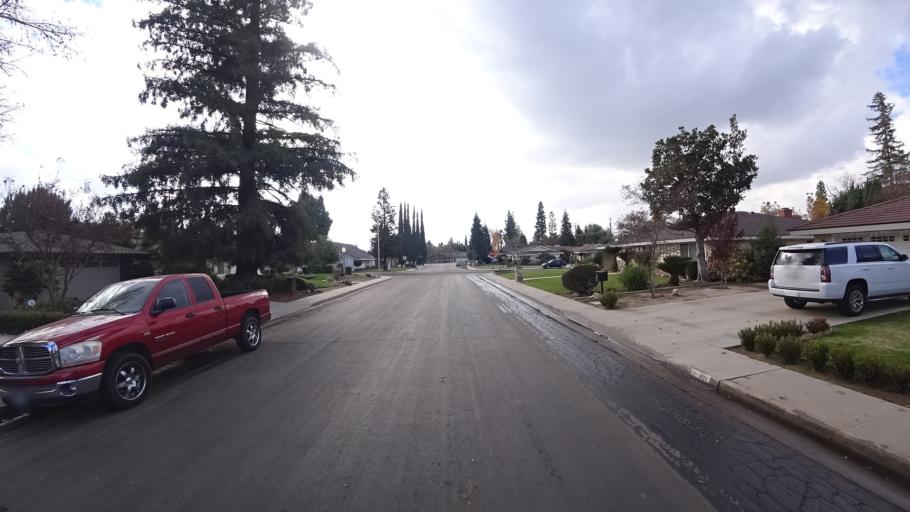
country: US
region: California
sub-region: Kern County
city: Greenacres
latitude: 35.3493
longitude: -119.0838
